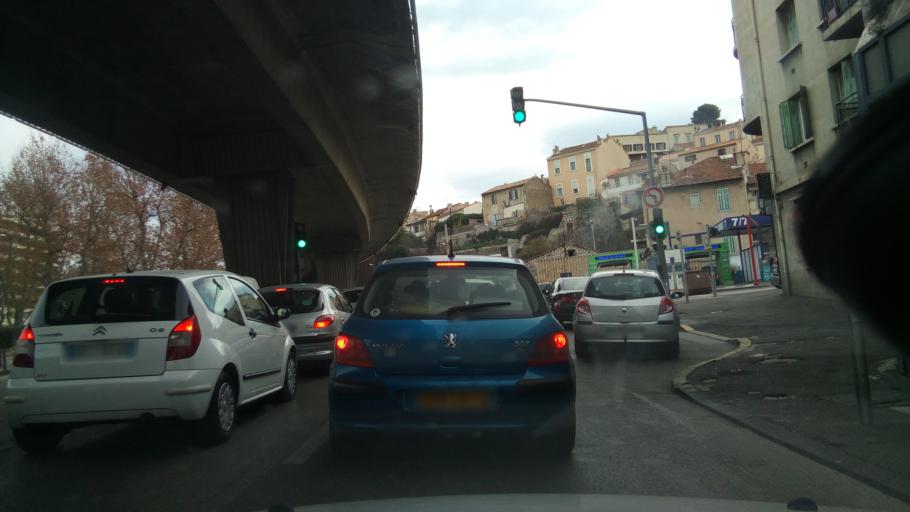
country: FR
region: Provence-Alpes-Cote d'Azur
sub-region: Departement des Bouches-du-Rhone
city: Marseille 01
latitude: 43.3140
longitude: 5.3883
